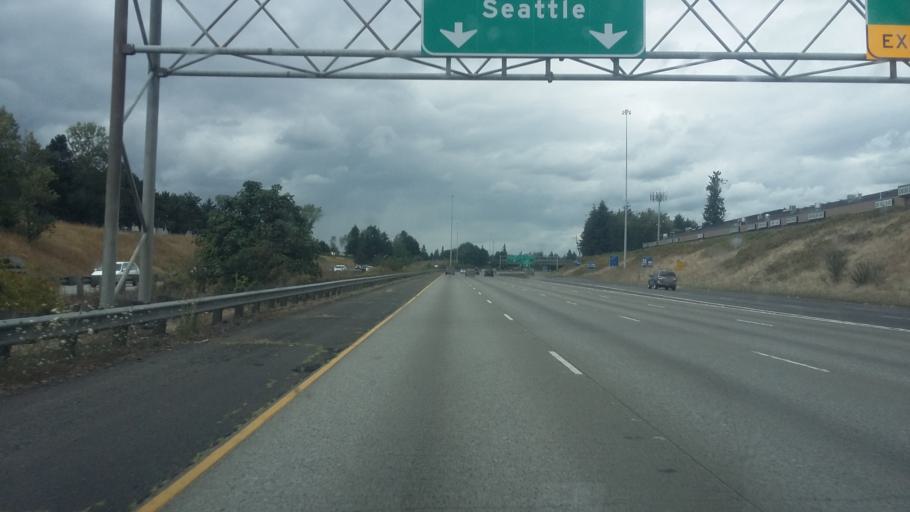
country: US
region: Washington
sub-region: Clark County
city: Orchards
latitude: 45.6154
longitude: -122.5552
